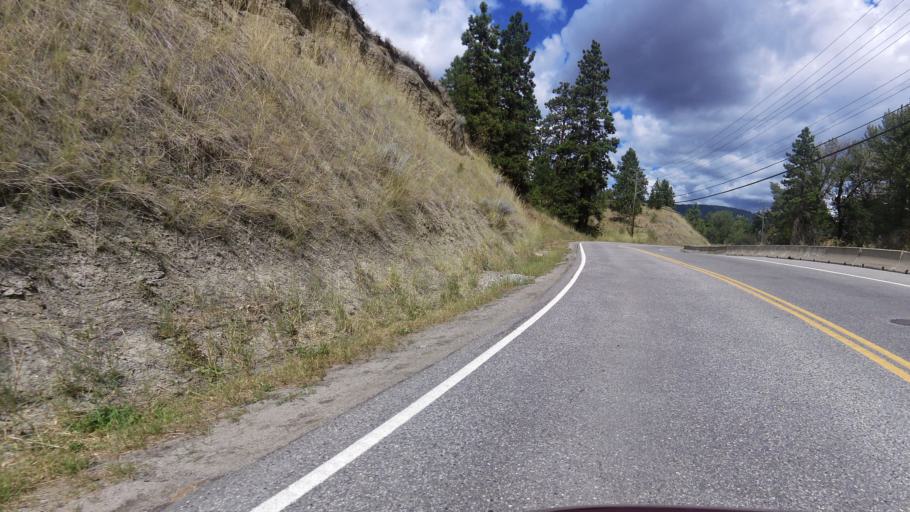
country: CA
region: British Columbia
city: West Kelowna
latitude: 49.8251
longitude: -119.6178
